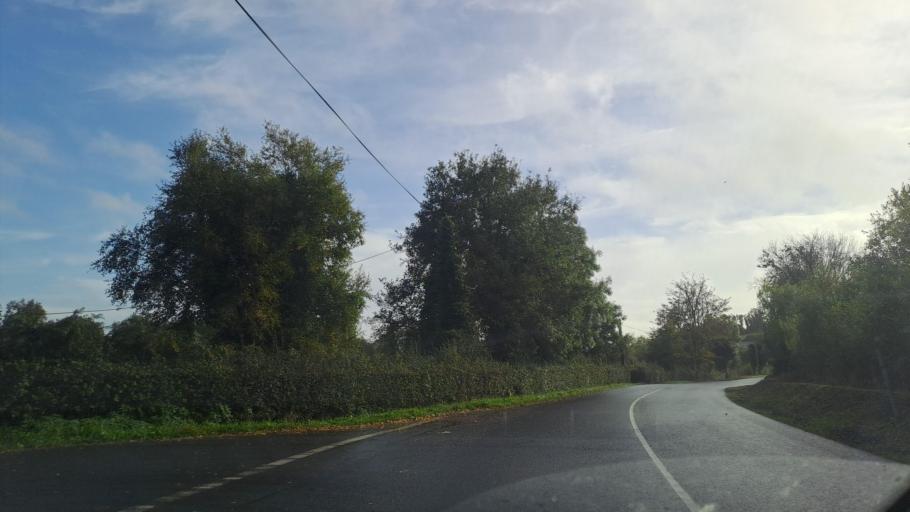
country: IE
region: Ulster
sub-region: County Monaghan
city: Carrickmacross
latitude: 53.9080
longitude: -6.7023
